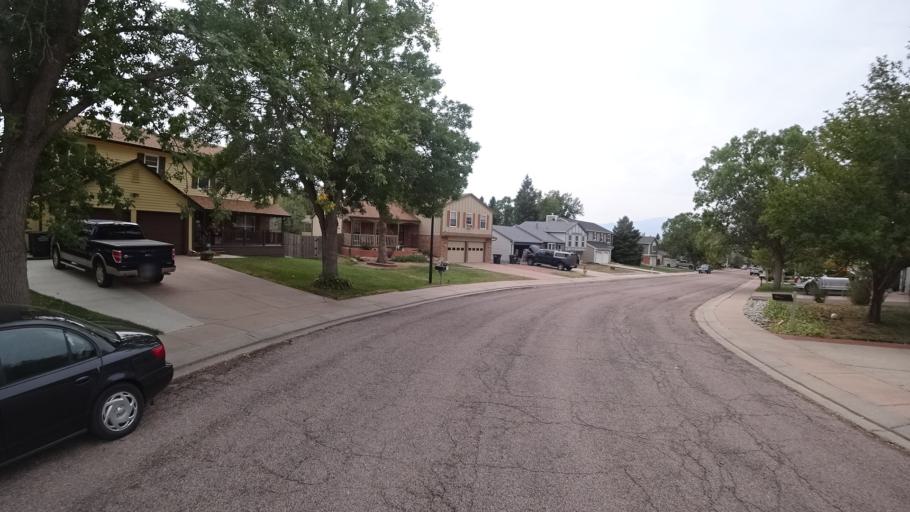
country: US
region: Colorado
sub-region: El Paso County
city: Cimarron Hills
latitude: 38.9020
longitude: -104.7303
